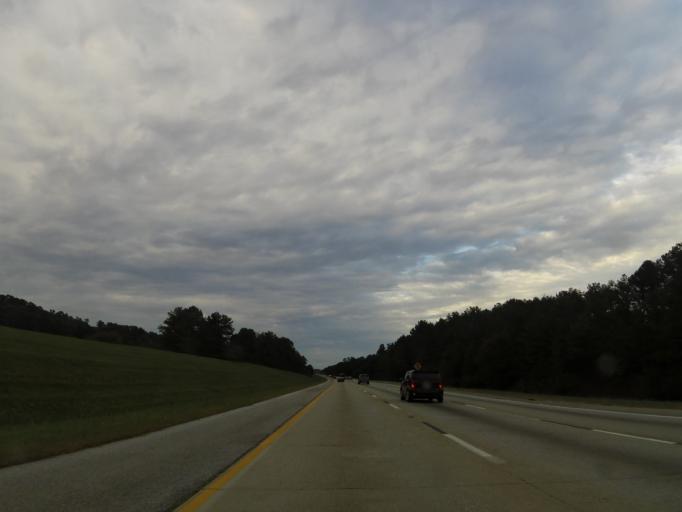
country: US
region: Alabama
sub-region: Jefferson County
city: Vestavia Hills
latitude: 33.4130
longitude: -86.7577
